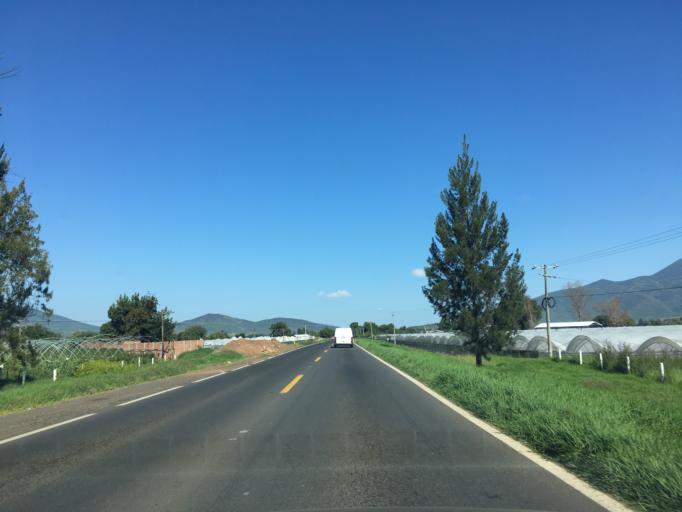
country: MX
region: Mexico
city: Tangancicuaro de Arista
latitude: 19.8660
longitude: -102.1910
